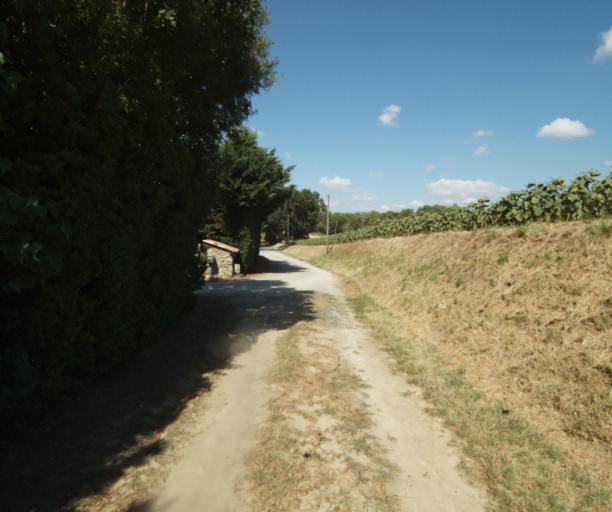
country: FR
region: Midi-Pyrenees
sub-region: Departement de la Haute-Garonne
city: Caraman
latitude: 43.4689
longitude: 1.7853
